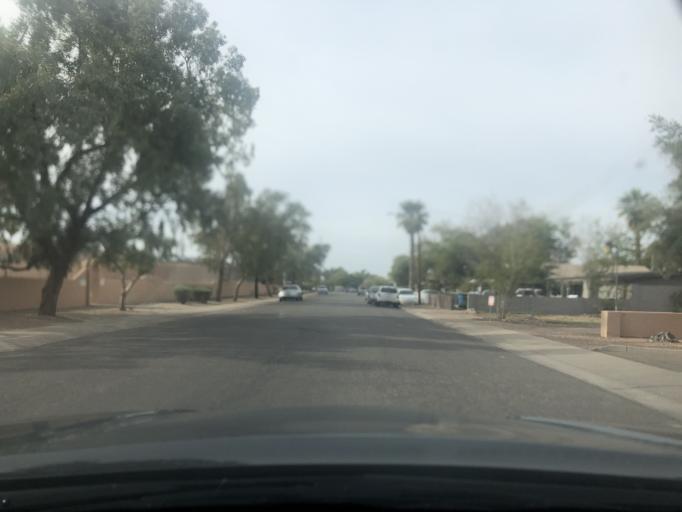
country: US
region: Arizona
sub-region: Maricopa County
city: Phoenix
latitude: 33.4596
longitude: -112.0414
